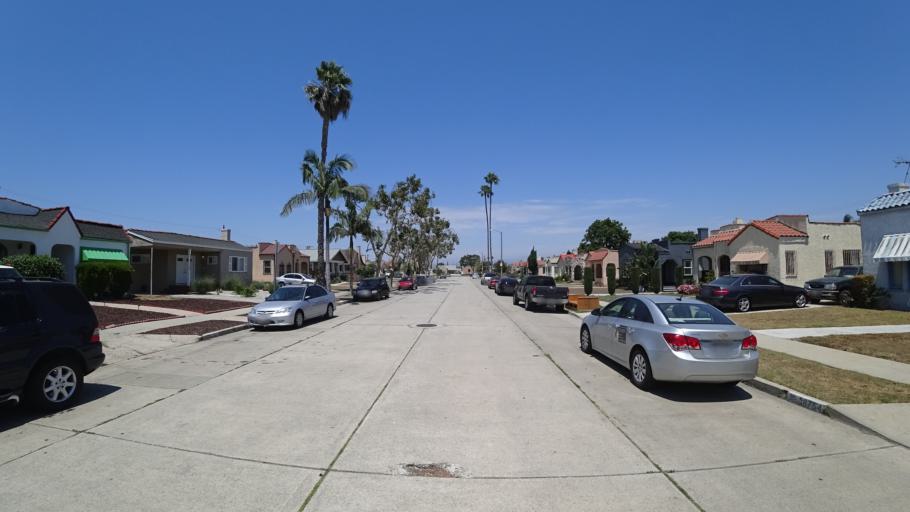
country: US
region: California
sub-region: Los Angeles County
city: Westmont
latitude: 33.9573
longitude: -118.3036
